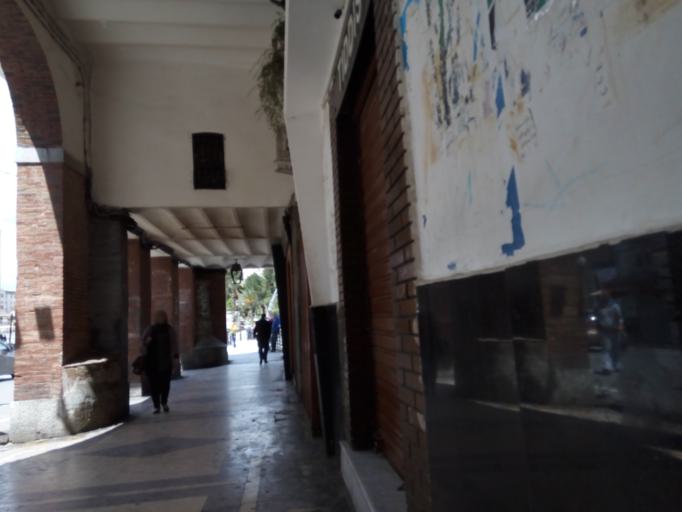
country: DZ
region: Constantine
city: Constantine
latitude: 36.3629
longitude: 6.6083
